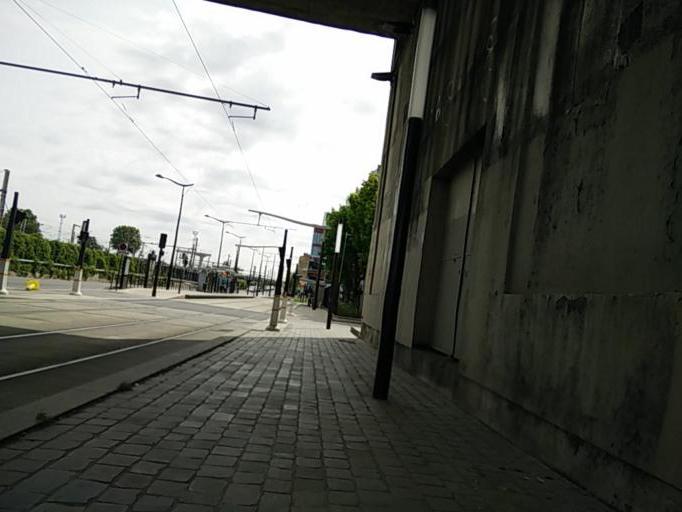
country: FR
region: Ile-de-France
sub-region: Departement de Seine-Saint-Denis
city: Pantin
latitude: 48.8974
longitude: 2.3942
